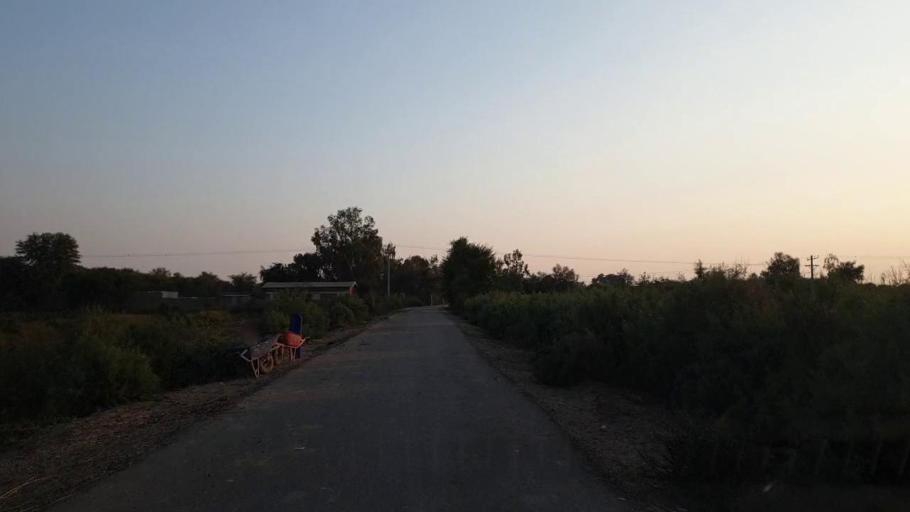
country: PK
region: Sindh
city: Sehwan
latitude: 26.4499
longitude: 67.7679
